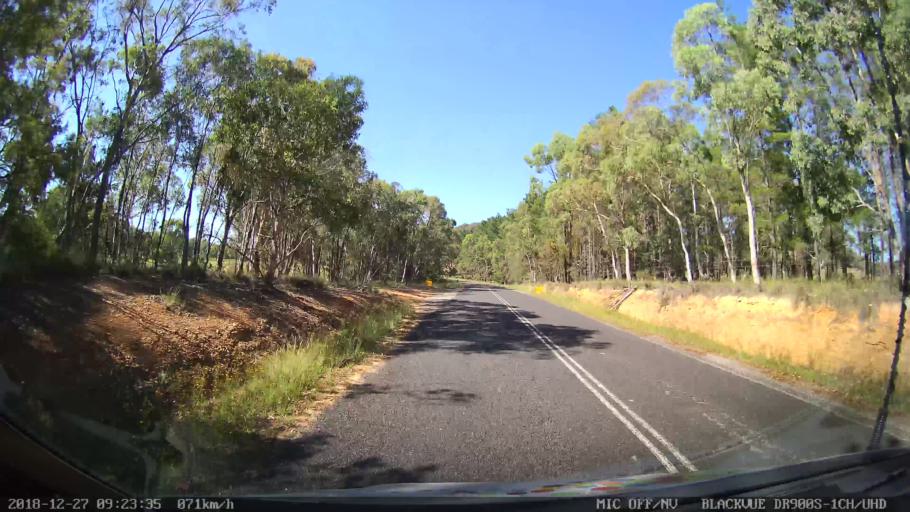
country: AU
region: New South Wales
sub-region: Lithgow
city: Portland
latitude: -33.1274
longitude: 149.9965
